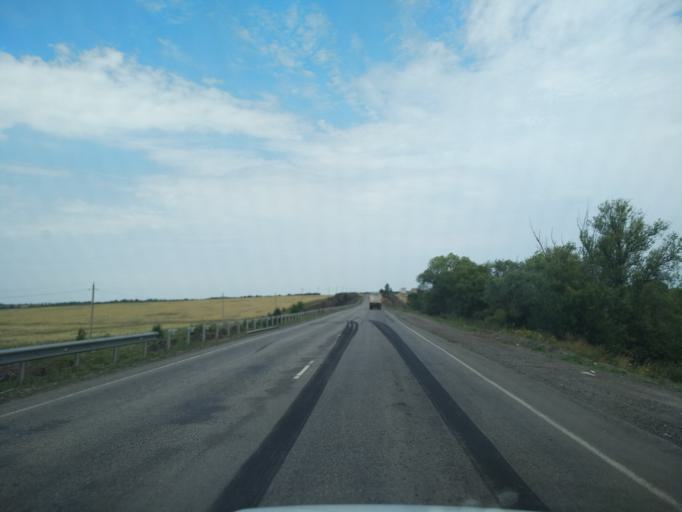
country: RU
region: Voronezj
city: Verkhnyaya Khava
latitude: 51.6753
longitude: 39.8155
